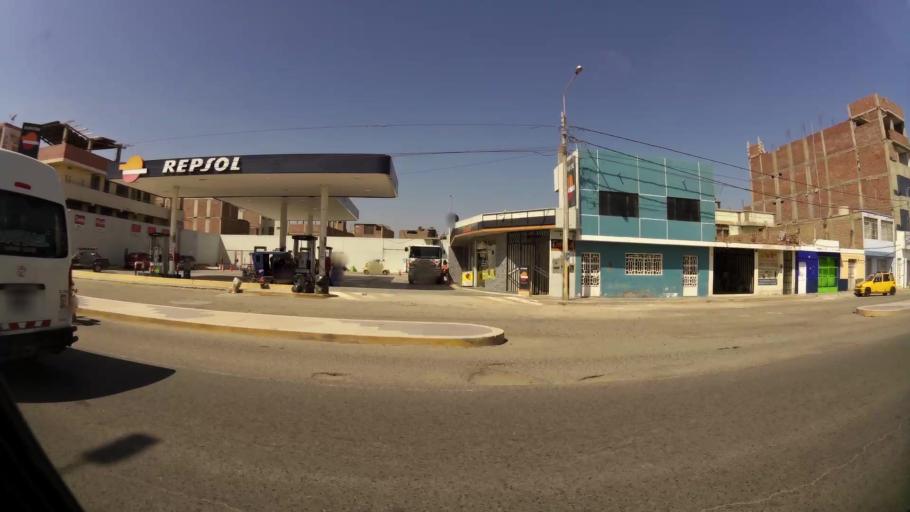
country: PE
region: Lambayeque
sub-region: Provincia de Chiclayo
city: Chiclayo
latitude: -6.7816
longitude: -79.8331
